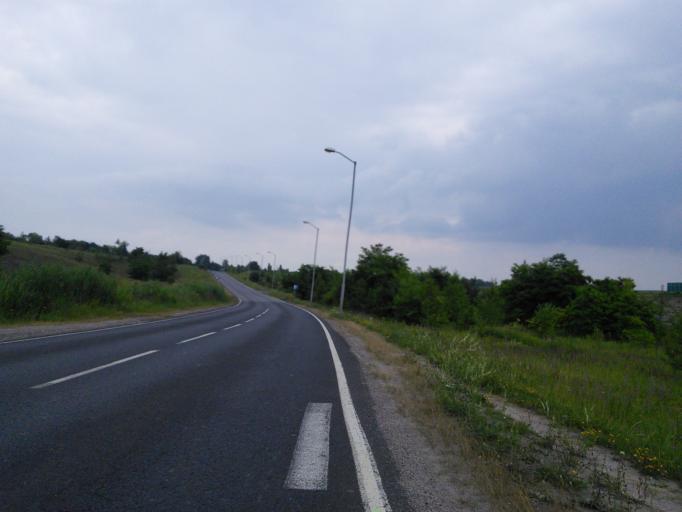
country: PL
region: Silesian Voivodeship
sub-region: Piekary Slaskie
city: Piekary Slaskie
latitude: 50.3692
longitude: 18.9468
